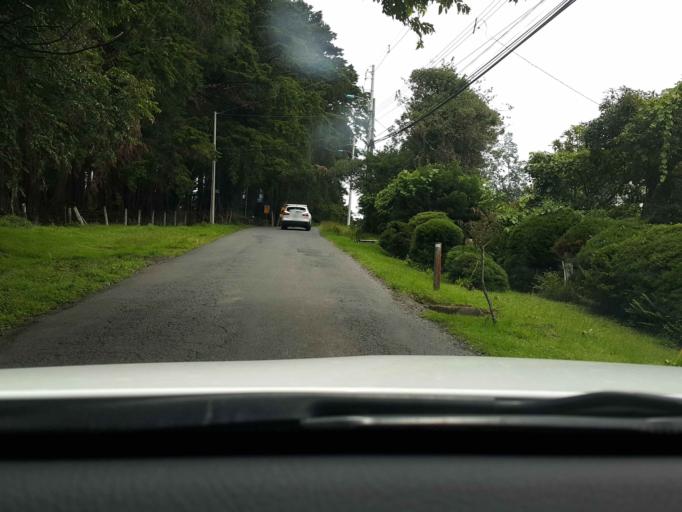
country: CR
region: Heredia
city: San Josecito
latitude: 10.0598
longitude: -84.0911
